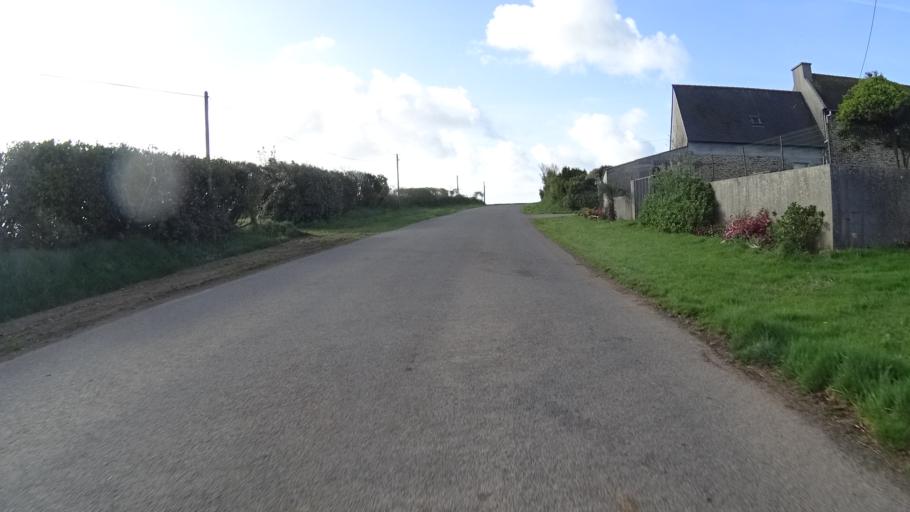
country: FR
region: Brittany
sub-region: Departement du Finistere
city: Plouzane
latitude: 48.3917
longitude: -4.6622
